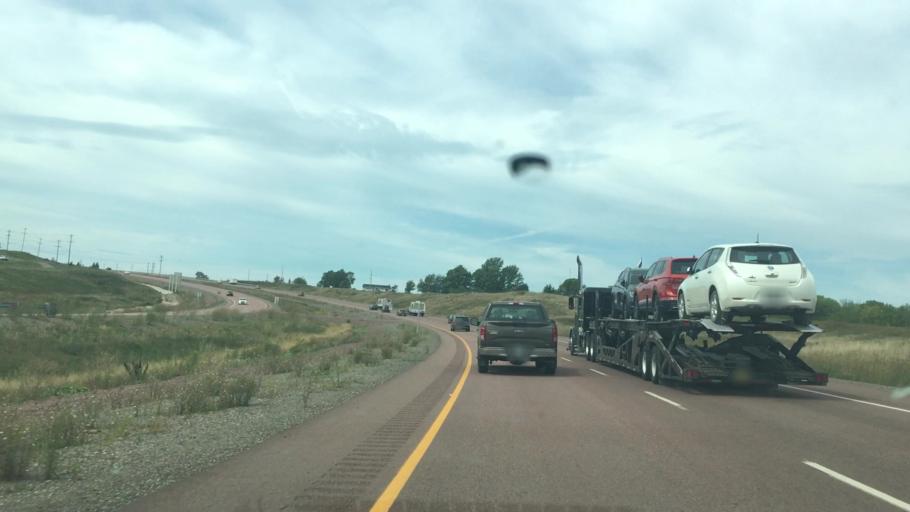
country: CA
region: Nova Scotia
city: Antigonish
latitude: 45.6040
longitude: -61.9200
